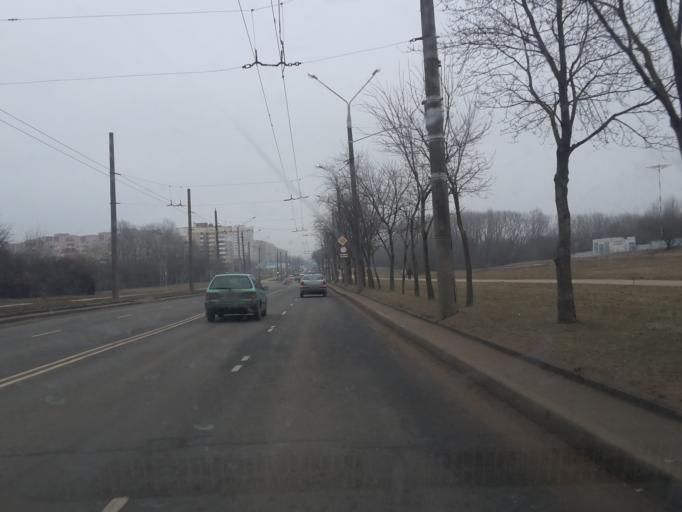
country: BY
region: Minsk
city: Novoye Medvezhino
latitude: 53.8938
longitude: 27.4693
